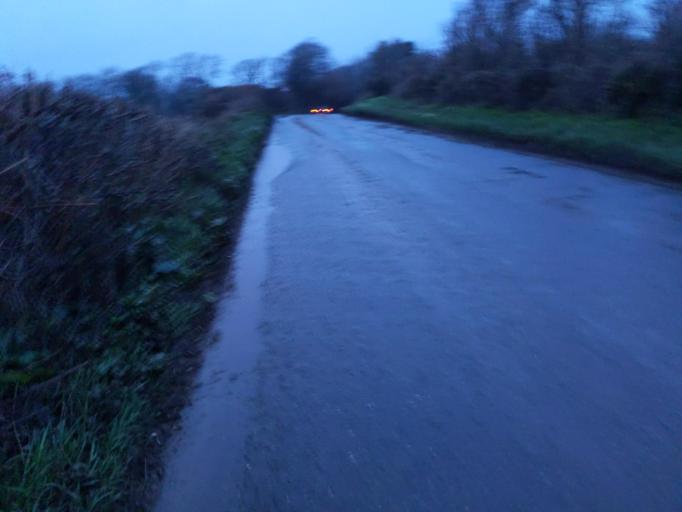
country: GB
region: England
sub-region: Devon
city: Yealmpton
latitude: 50.3359
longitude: -4.0148
